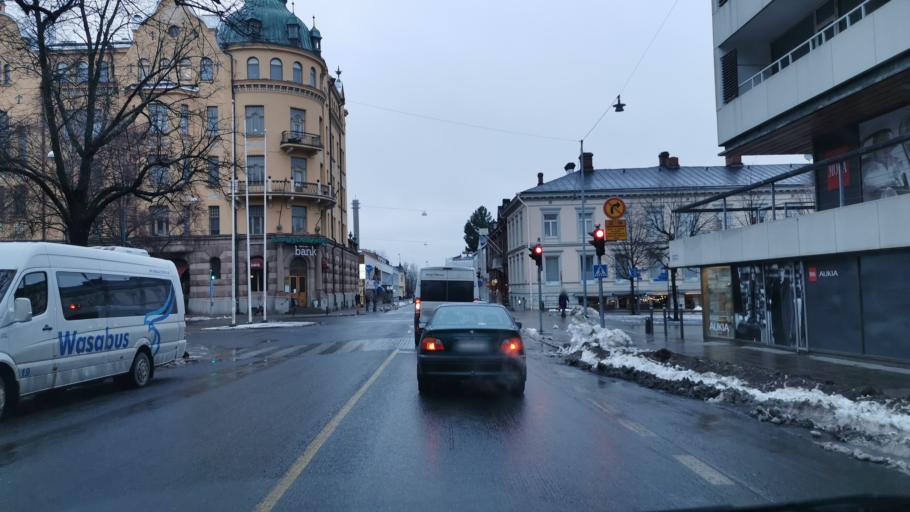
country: FI
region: Ostrobothnia
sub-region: Vaasa
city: Vaasa
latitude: 63.0955
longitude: 21.6129
